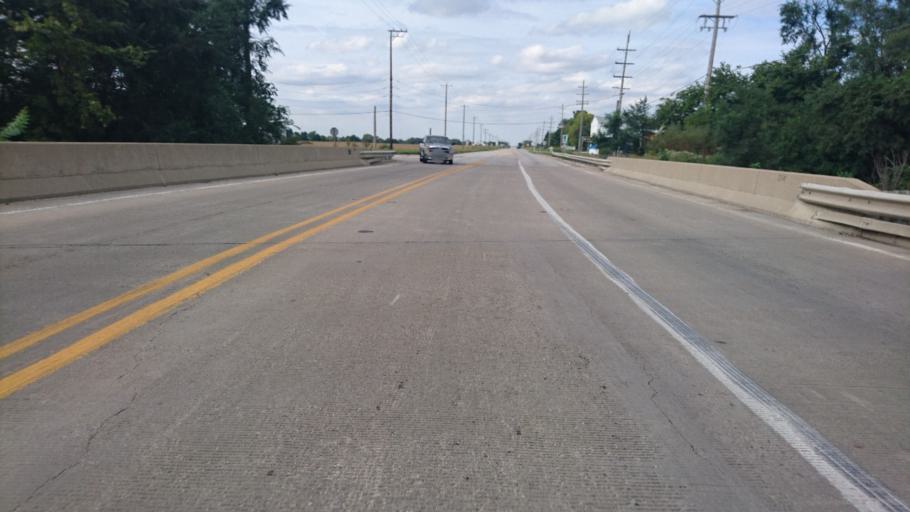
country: US
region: Illinois
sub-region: Livingston County
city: Pontiac
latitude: 40.8876
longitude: -88.6428
